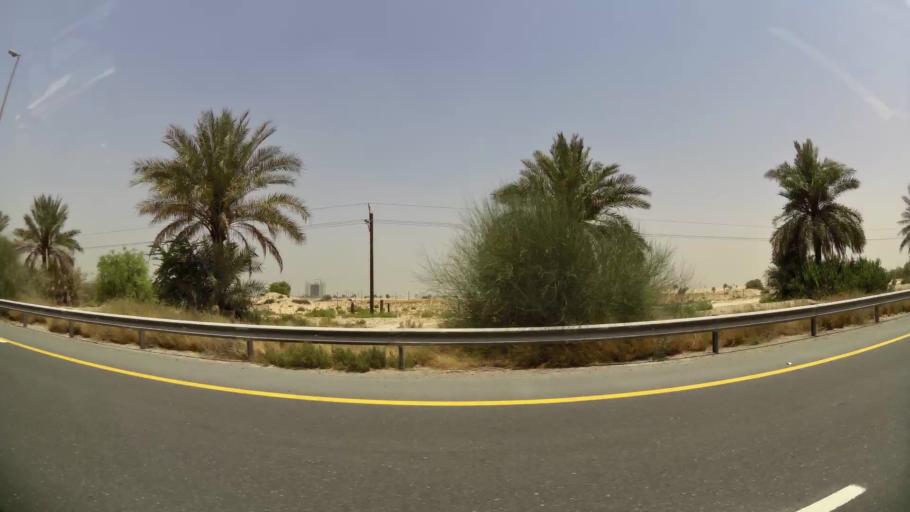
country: AE
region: Dubai
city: Dubai
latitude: 25.0571
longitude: 55.2563
